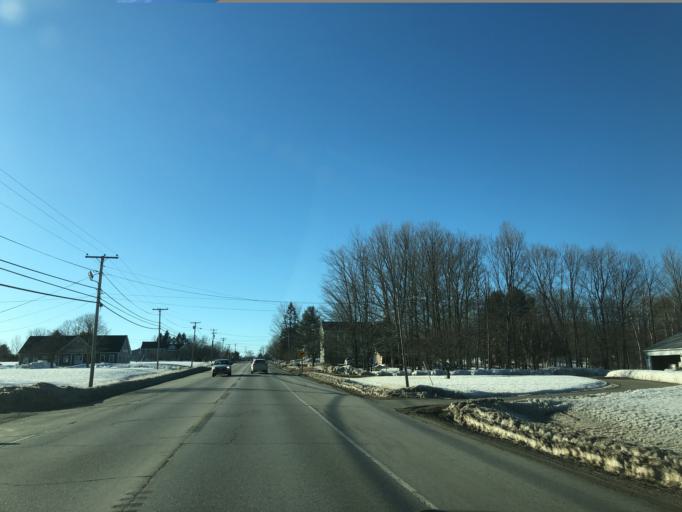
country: US
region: Maine
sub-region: Penobscot County
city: Charleston
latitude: 44.9871
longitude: -69.0099
